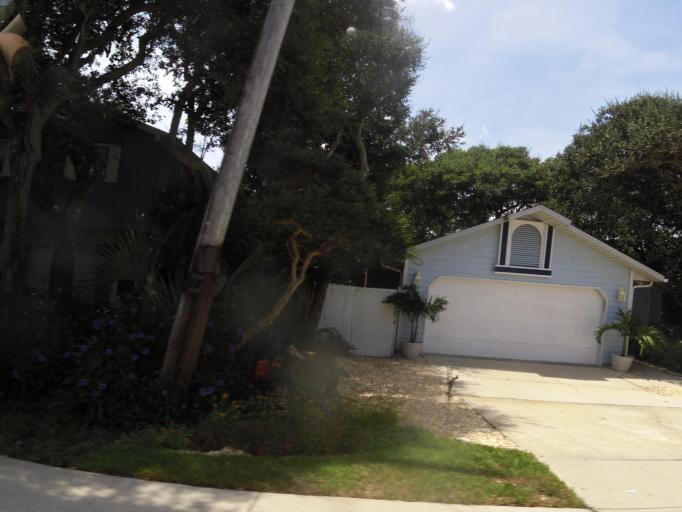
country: US
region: Florida
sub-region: Volusia County
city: Ponce Inlet
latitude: 29.0965
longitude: -80.9393
